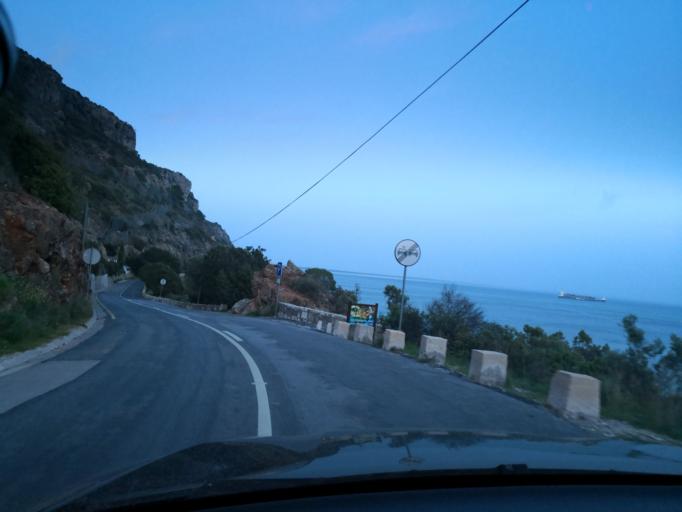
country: PT
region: Setubal
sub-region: Setubal
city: Setubal
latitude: 38.4849
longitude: -8.9621
